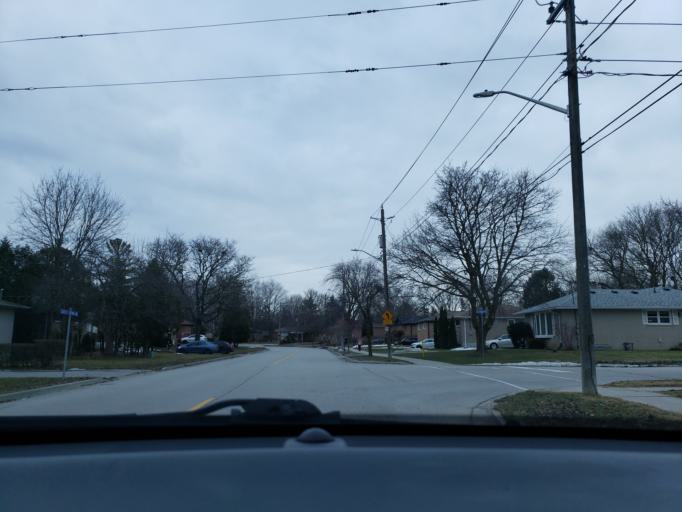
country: CA
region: Ontario
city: Newmarket
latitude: 44.0504
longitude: -79.4740
